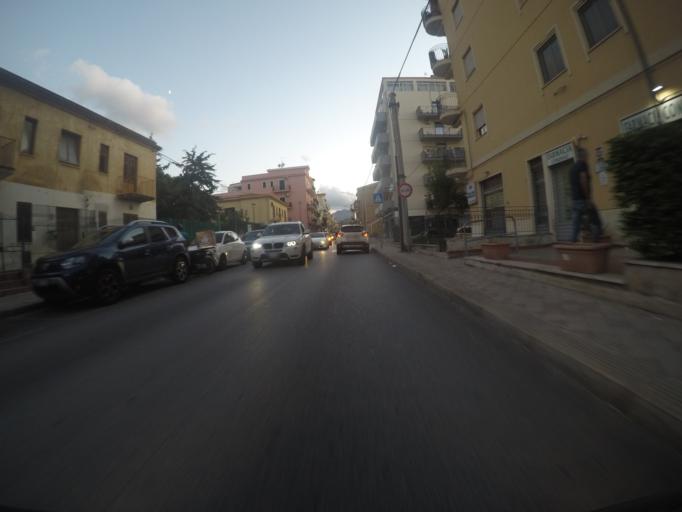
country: IT
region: Sicily
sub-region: Palermo
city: Capaci
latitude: 38.1762
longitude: 13.2425
